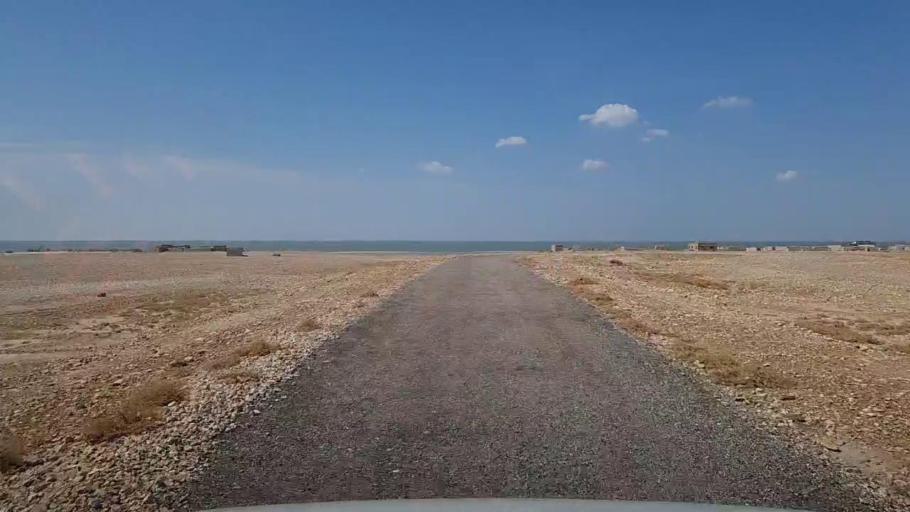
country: PK
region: Sindh
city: Bhan
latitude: 26.3844
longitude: 67.6297
